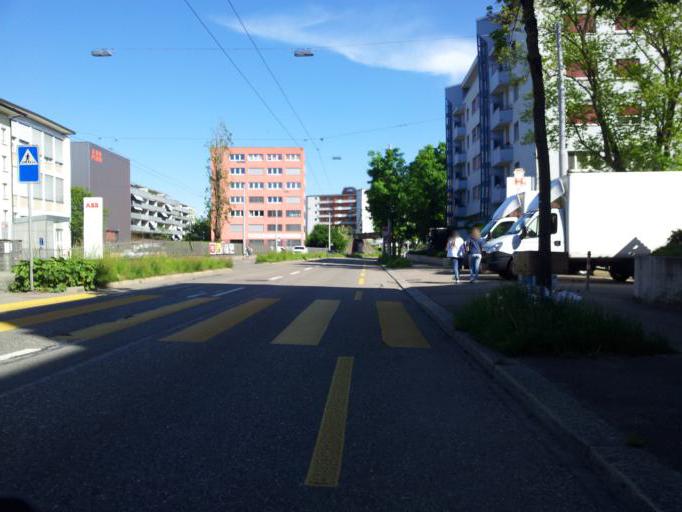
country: CH
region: Zurich
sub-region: Bezirk Zuerich
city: Zuerich (Kreis 9) / Altstetten
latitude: 47.3925
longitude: 8.4763
